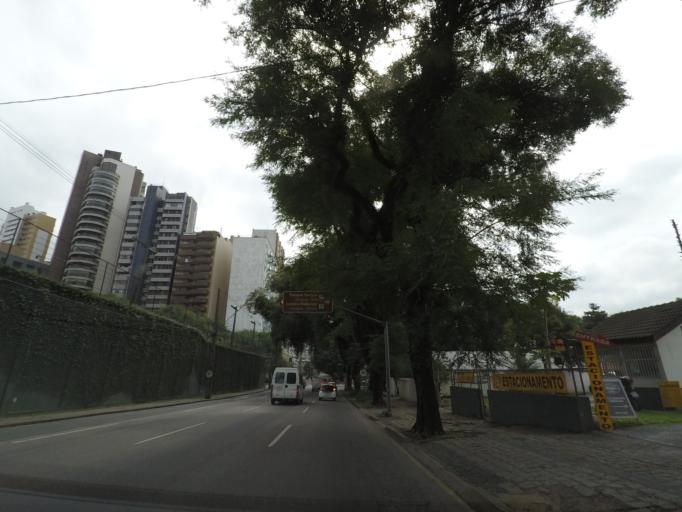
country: BR
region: Parana
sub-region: Curitiba
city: Curitiba
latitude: -25.4510
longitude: -49.2850
